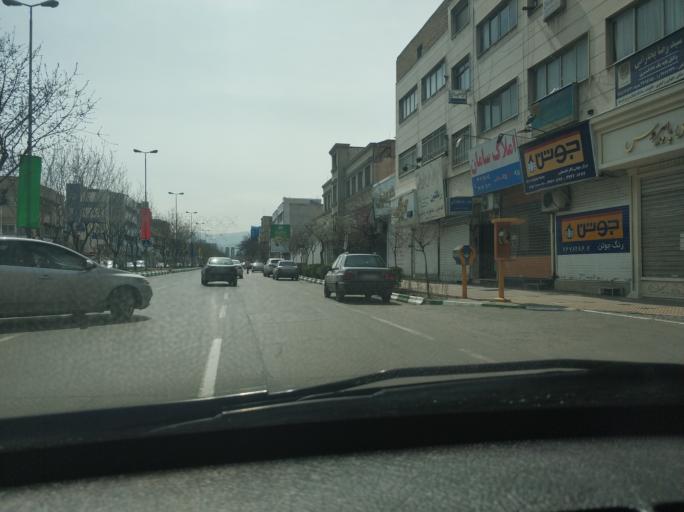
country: IR
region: Razavi Khorasan
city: Mashhad
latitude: 36.3038
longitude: 59.5650
